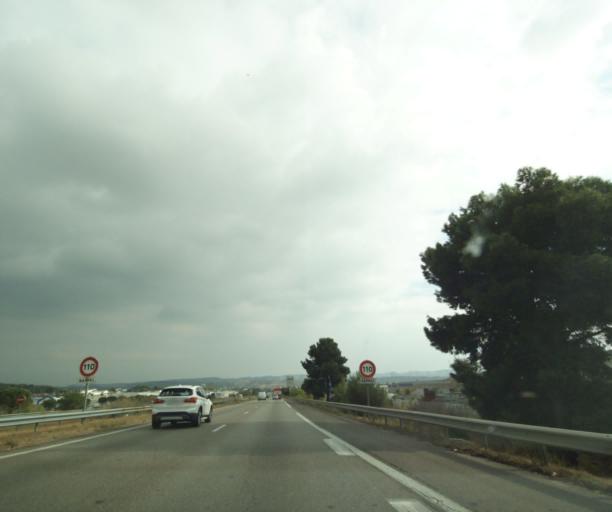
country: FR
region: Provence-Alpes-Cote d'Azur
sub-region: Departement des Bouches-du-Rhone
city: Vitrolles
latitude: 43.4358
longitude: 5.2538
